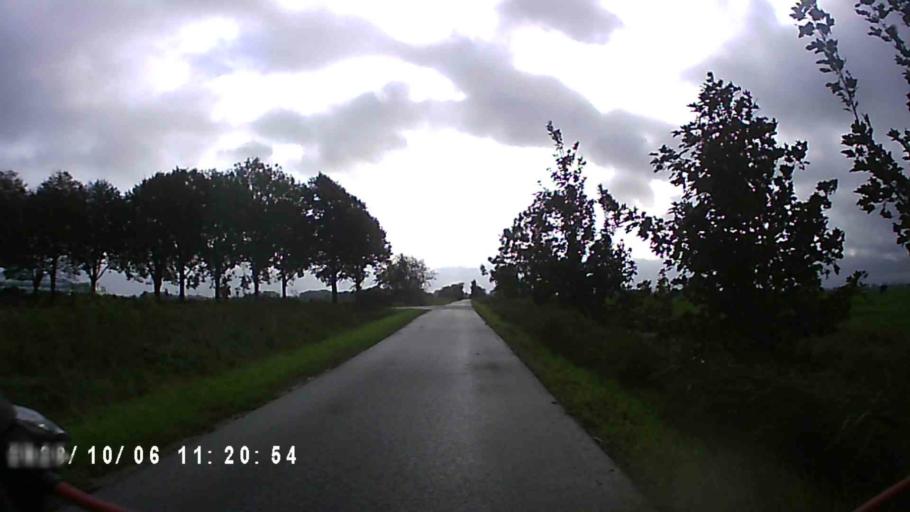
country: NL
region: Groningen
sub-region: Gemeente Zuidhorn
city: Oldehove
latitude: 53.3487
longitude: 6.4051
